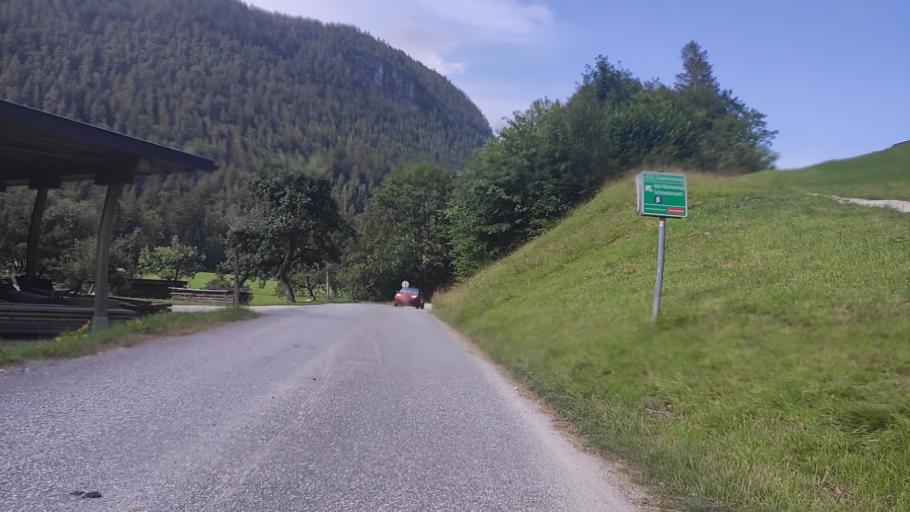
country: DE
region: Bavaria
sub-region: Upper Bavaria
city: Schneizlreuth
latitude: 47.6640
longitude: 12.7652
